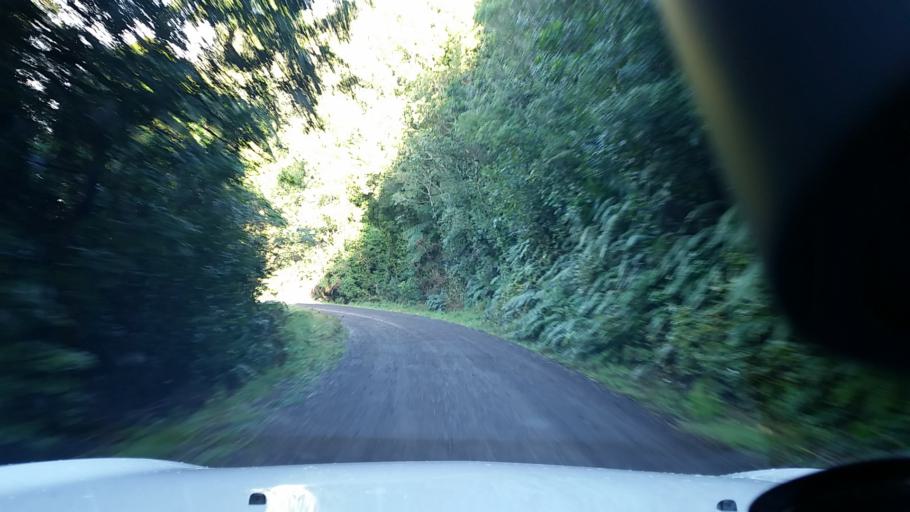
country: NZ
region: Bay of Plenty
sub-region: Kawerau District
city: Kawerau
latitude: -38.0232
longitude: 176.5670
